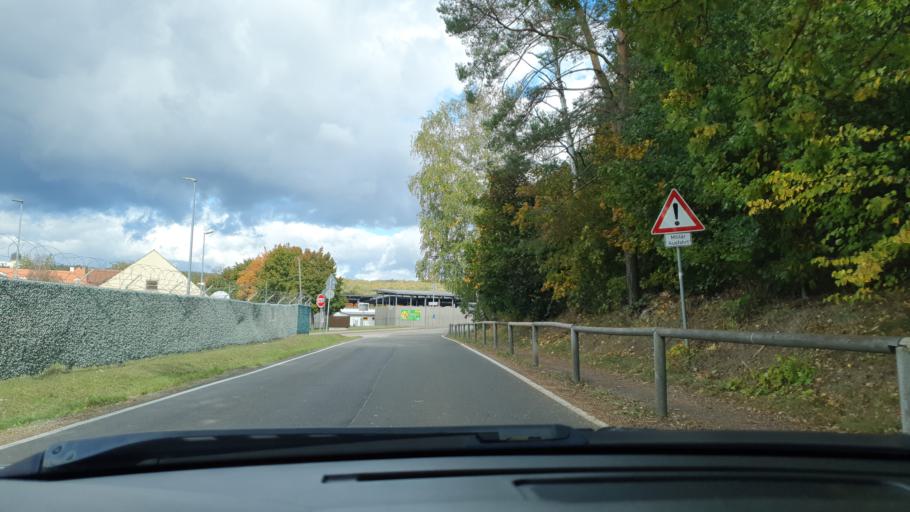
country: DE
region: Rheinland-Pfalz
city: Kaiserslautern
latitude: 49.4397
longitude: 7.8095
